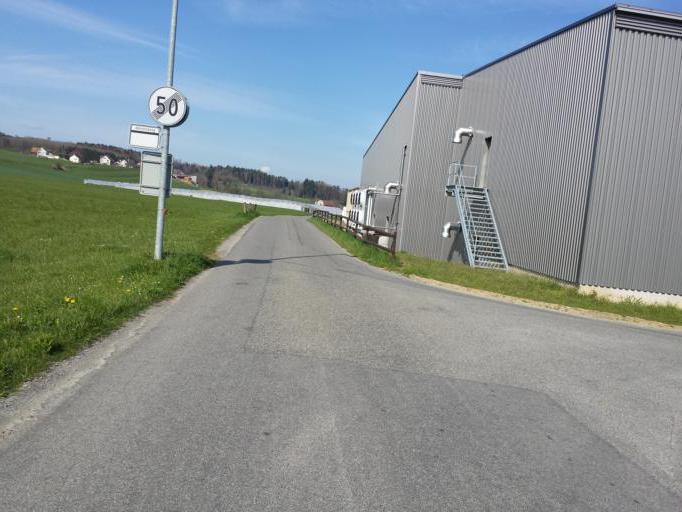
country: CH
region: Saint Gallen
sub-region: Wahlkreis St. Gallen
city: Muolen
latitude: 47.5346
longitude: 9.3398
